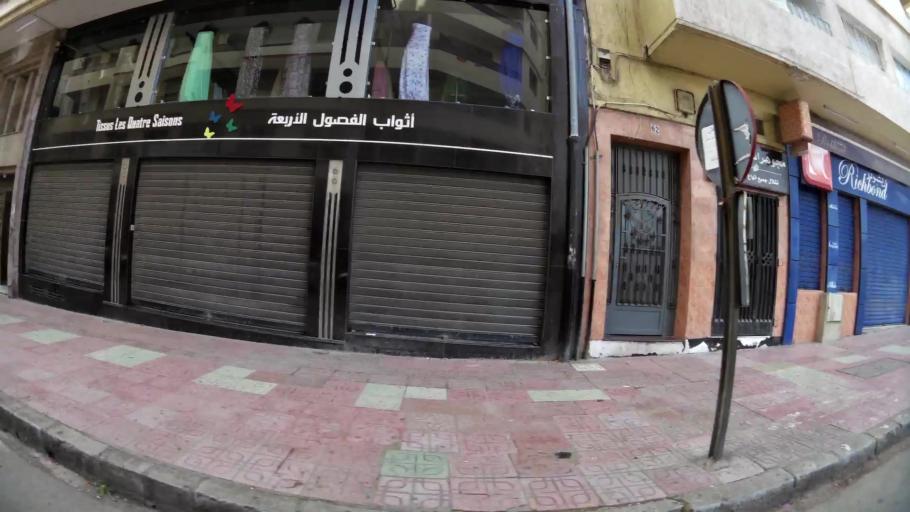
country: MA
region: Tanger-Tetouan
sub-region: Tanger-Assilah
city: Tangier
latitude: 35.7764
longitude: -5.8141
